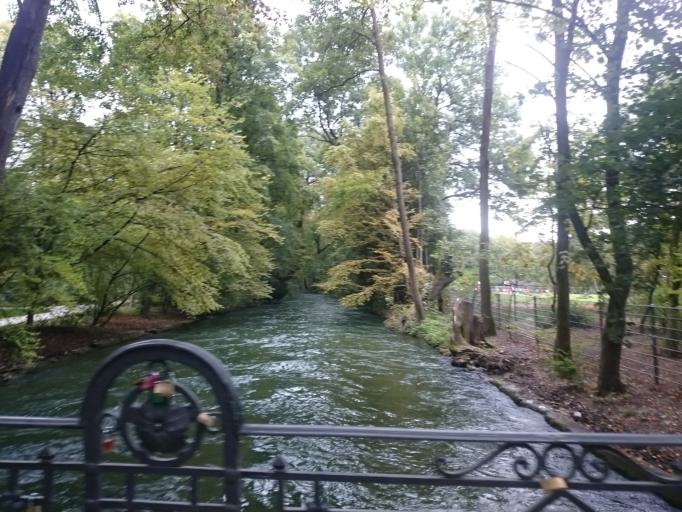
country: DE
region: Bavaria
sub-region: Upper Bavaria
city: Munich
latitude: 48.1453
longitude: 11.5884
